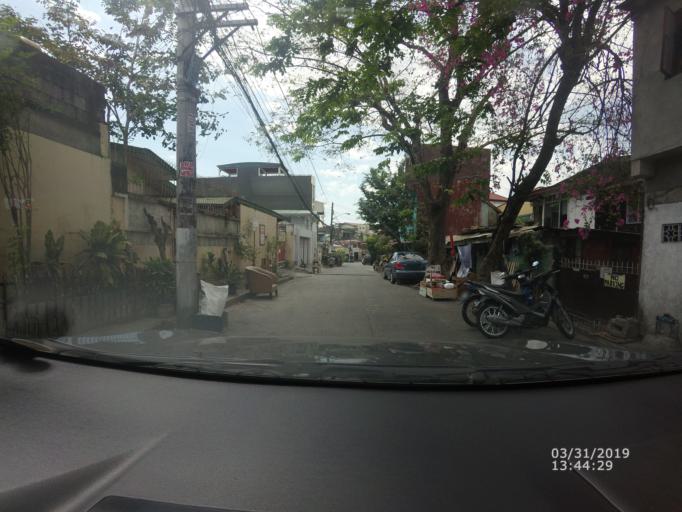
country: PH
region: Metro Manila
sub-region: Mandaluyong
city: Mandaluyong City
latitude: 14.5817
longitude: 121.0480
